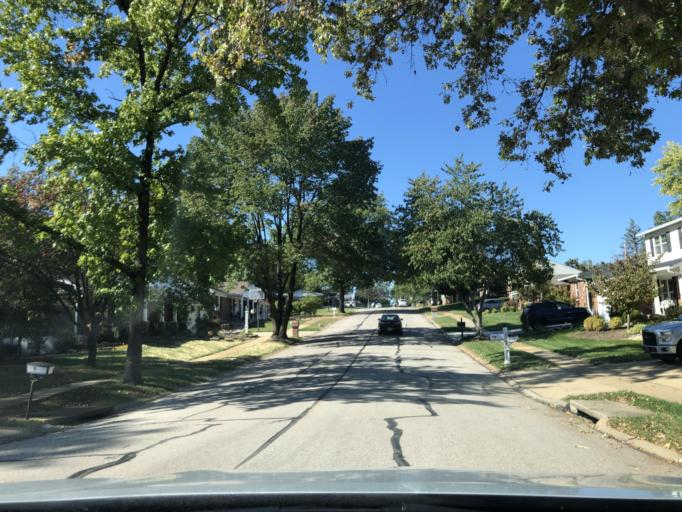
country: US
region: Missouri
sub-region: Saint Louis County
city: Concord
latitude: 38.5006
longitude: -90.3729
